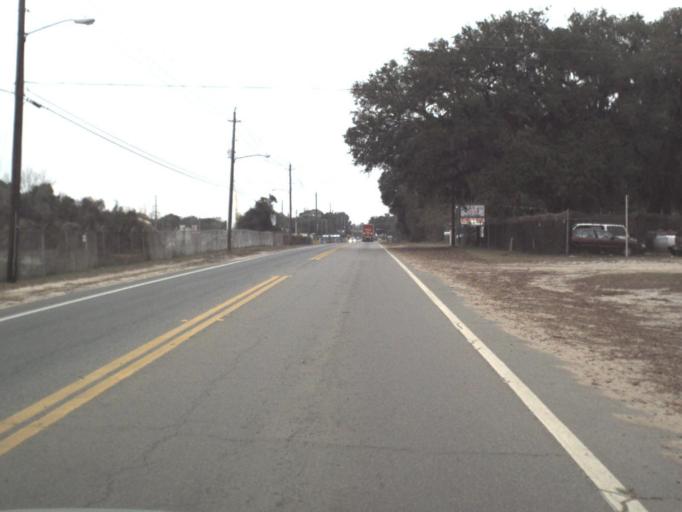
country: US
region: Florida
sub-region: Bay County
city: Springfield
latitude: 30.1407
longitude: -85.6157
